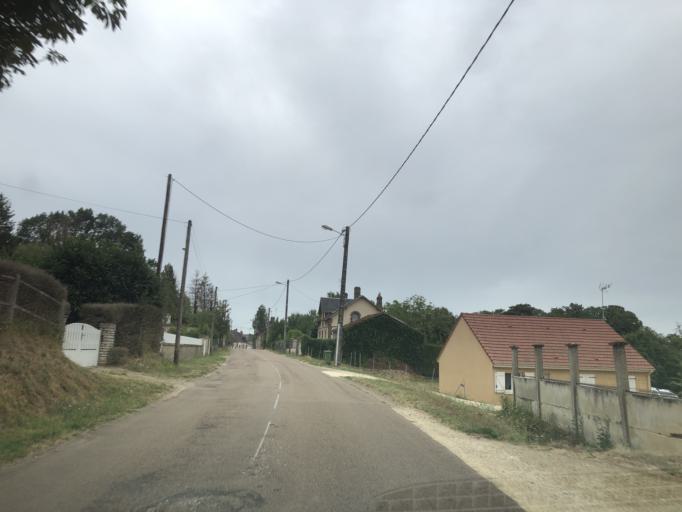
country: FR
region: Bourgogne
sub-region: Departement de l'Yonne
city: Charny
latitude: 47.9423
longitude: 3.1299
